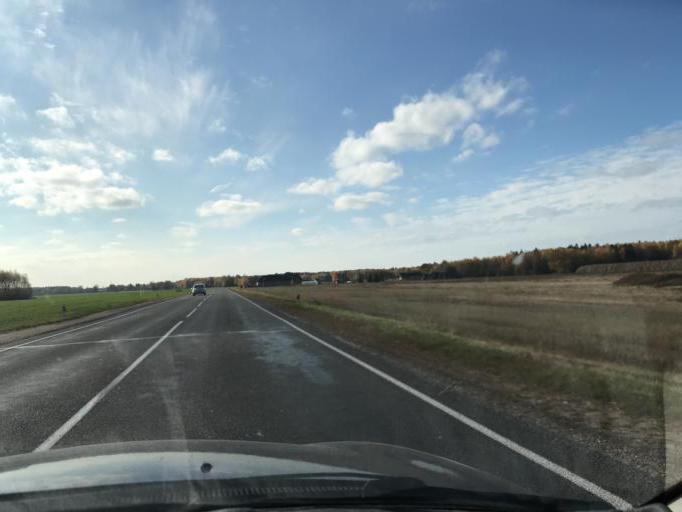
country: BY
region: Grodnenskaya
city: Voranava
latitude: 54.1902
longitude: 25.3433
